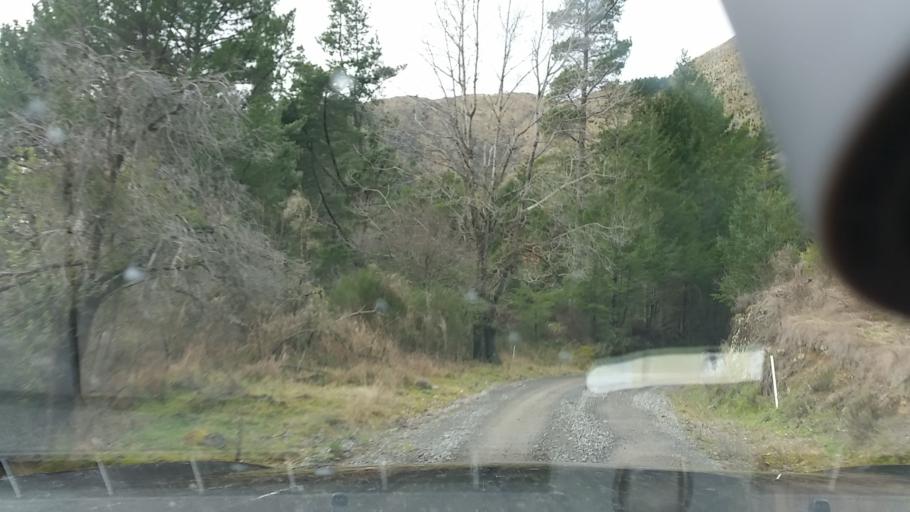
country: NZ
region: Tasman
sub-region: Tasman District
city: Richmond
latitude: -41.7300
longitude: 173.4678
